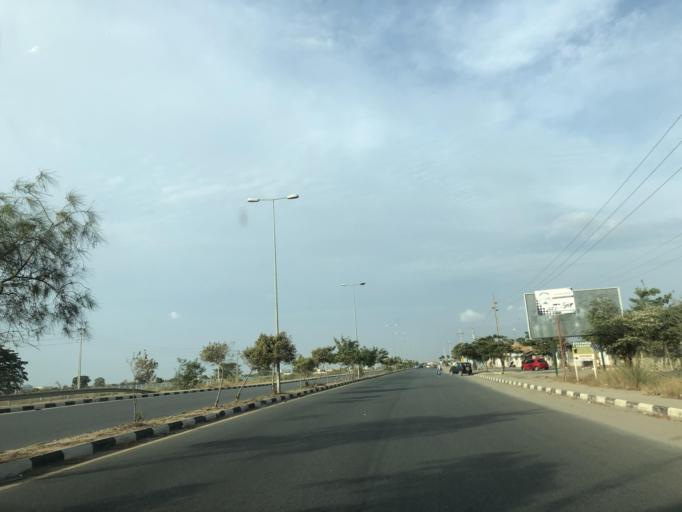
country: AO
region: Luanda
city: Luanda
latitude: -8.9377
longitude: 13.2964
